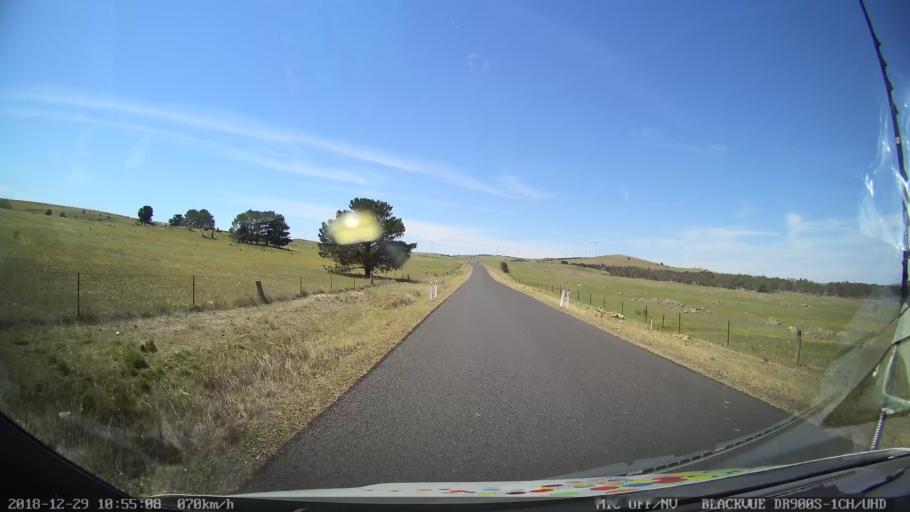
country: AU
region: New South Wales
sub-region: Palerang
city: Bungendore
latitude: -35.1207
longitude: 149.5308
